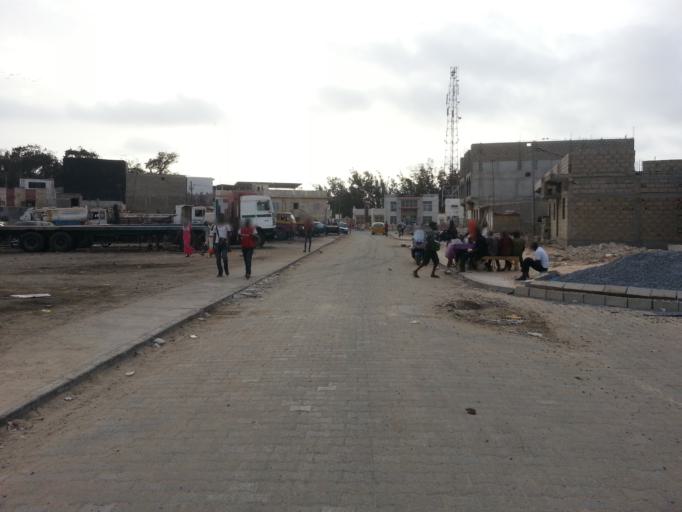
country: SN
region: Dakar
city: Pikine
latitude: 14.7690
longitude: -17.3869
